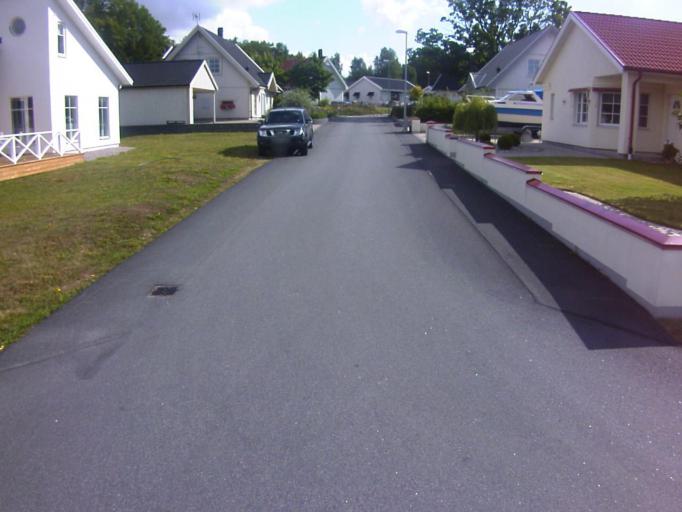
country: SE
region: Blekinge
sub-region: Solvesborgs Kommun
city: Soelvesborg
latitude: 56.0586
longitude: 14.5685
